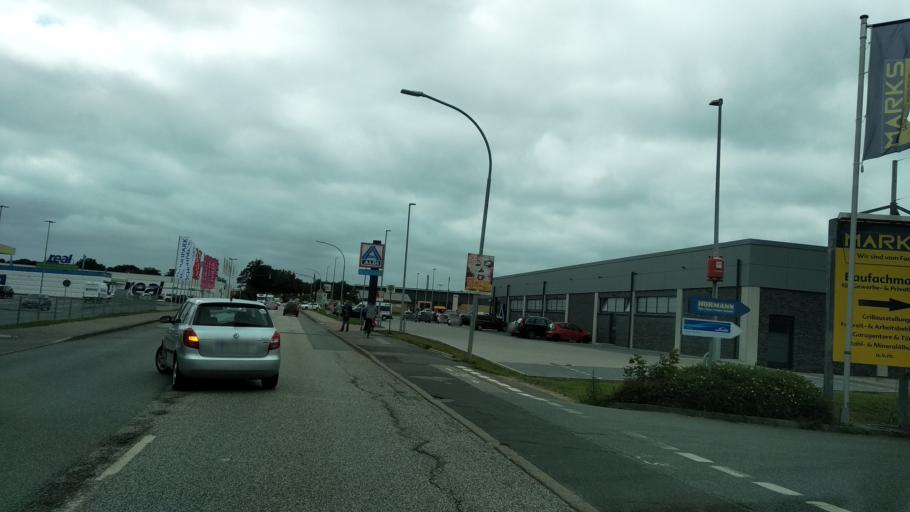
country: DE
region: Schleswig-Holstein
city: Neuberend
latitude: 54.5291
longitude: 9.5317
